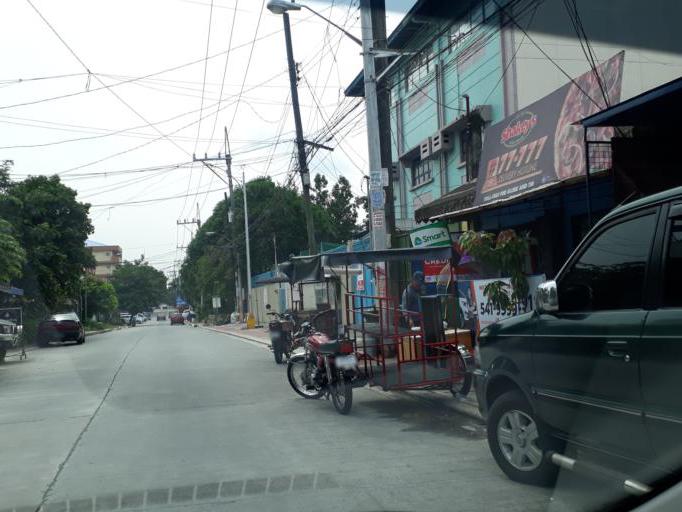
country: PH
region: Calabarzon
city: Del Monte
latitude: 14.6346
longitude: 121.0289
